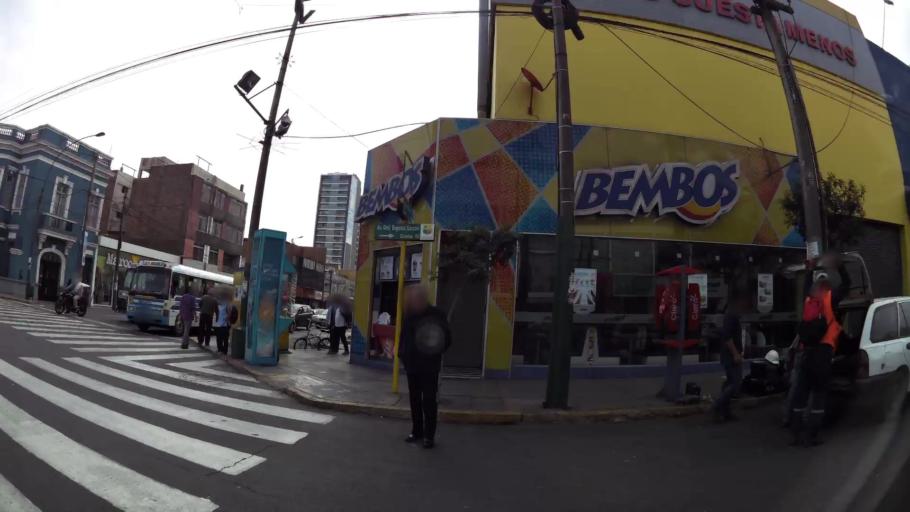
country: PE
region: Lima
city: Lima
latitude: -12.0758
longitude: -77.0527
